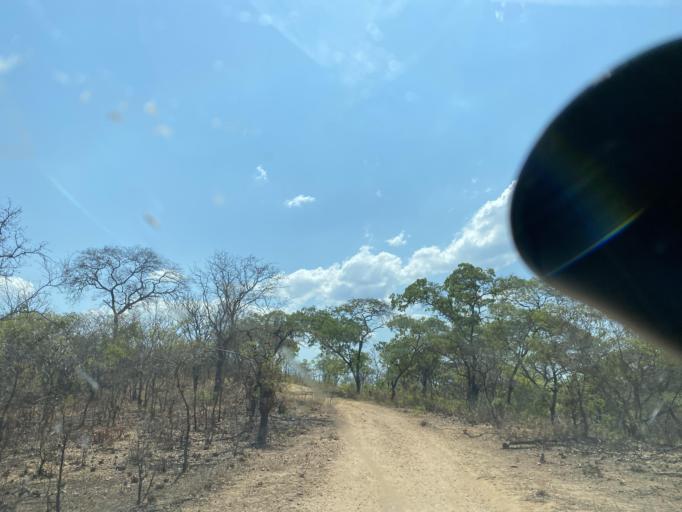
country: ZM
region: Lusaka
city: Chongwe
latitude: -15.0860
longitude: 29.4857
